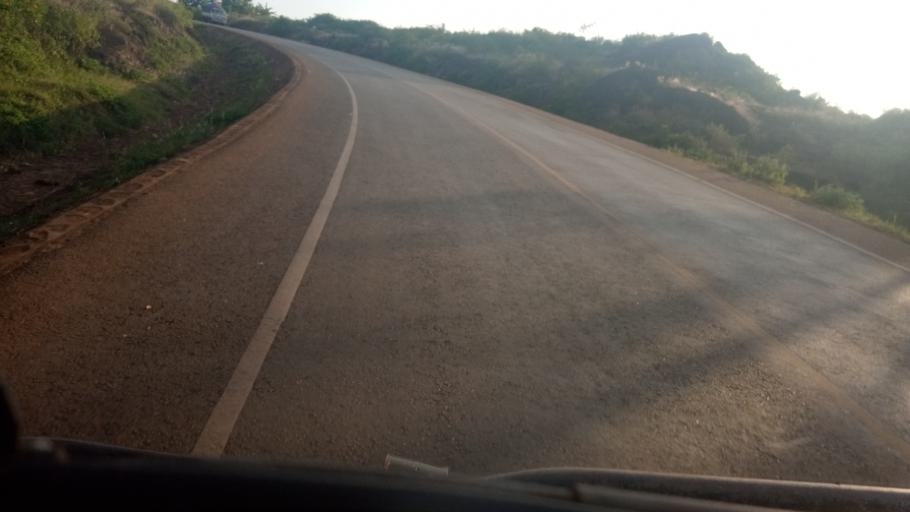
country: UG
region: Eastern Region
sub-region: Sironko District
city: Sironko
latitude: 1.3351
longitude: 34.3224
